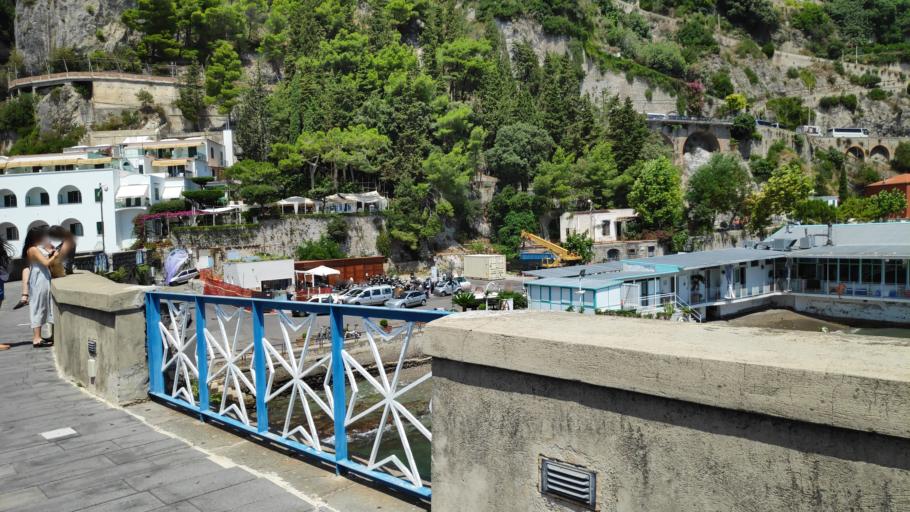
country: IT
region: Campania
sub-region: Provincia di Salerno
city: Amalfi
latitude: 40.6314
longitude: 14.5978
